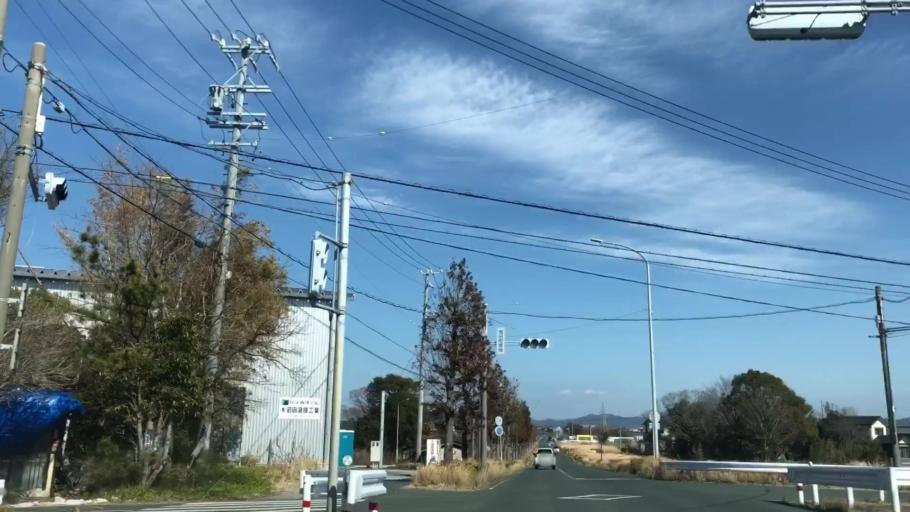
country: JP
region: Aichi
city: Toyohashi
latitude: 34.7144
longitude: 137.3625
